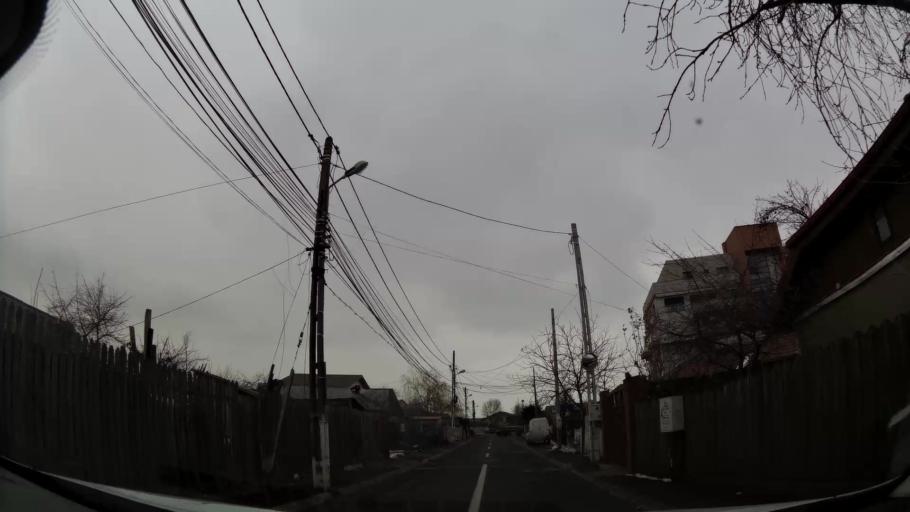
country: RO
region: Ilfov
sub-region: Comuna Otopeni
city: Otopeni
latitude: 44.5476
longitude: 26.0765
